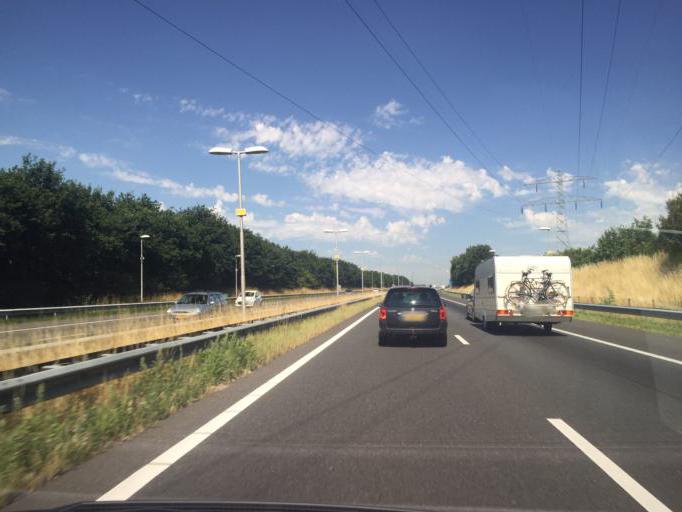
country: NL
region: North Brabant
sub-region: Gemeente Cuijk
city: Cuijk
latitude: 51.7273
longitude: 5.8552
